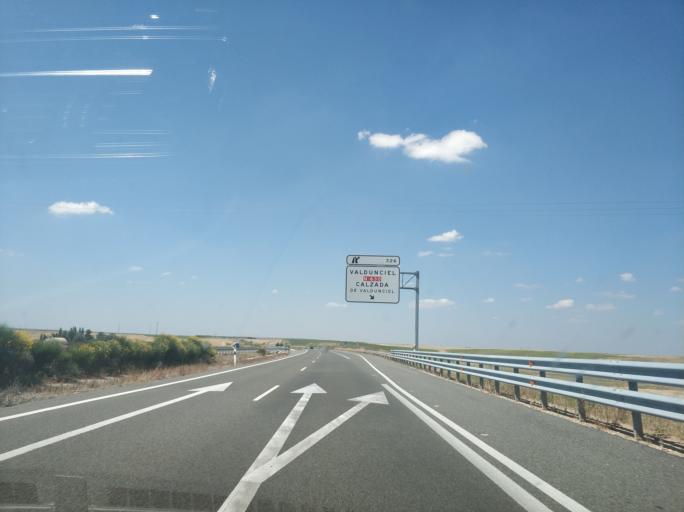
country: ES
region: Castille and Leon
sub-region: Provincia de Salamanca
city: Calzada de Valdunciel
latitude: 41.0824
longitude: -5.6881
